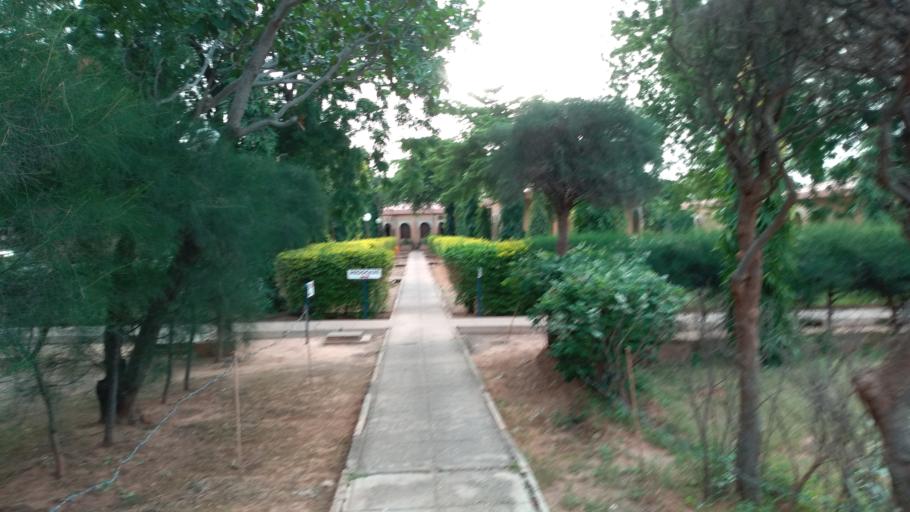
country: NG
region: Katsina
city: Katsina
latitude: 12.9617
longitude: 7.6390
